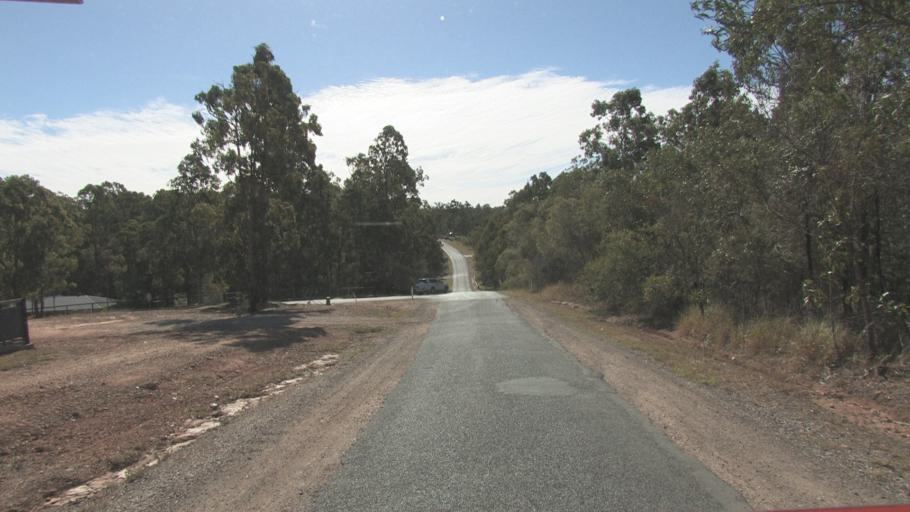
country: AU
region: Queensland
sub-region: Ipswich
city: Springfield Lakes
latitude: -27.7187
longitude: 152.9144
